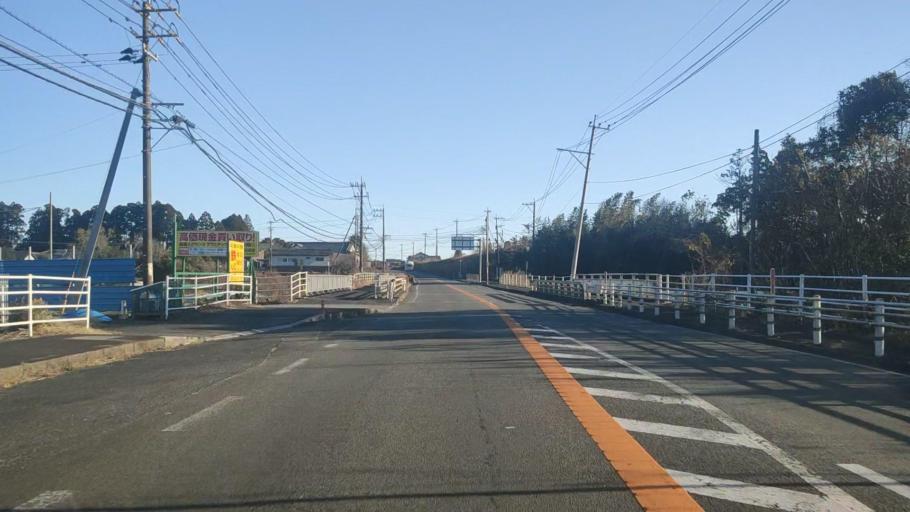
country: JP
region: Miyazaki
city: Takanabe
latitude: 32.3117
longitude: 131.5864
